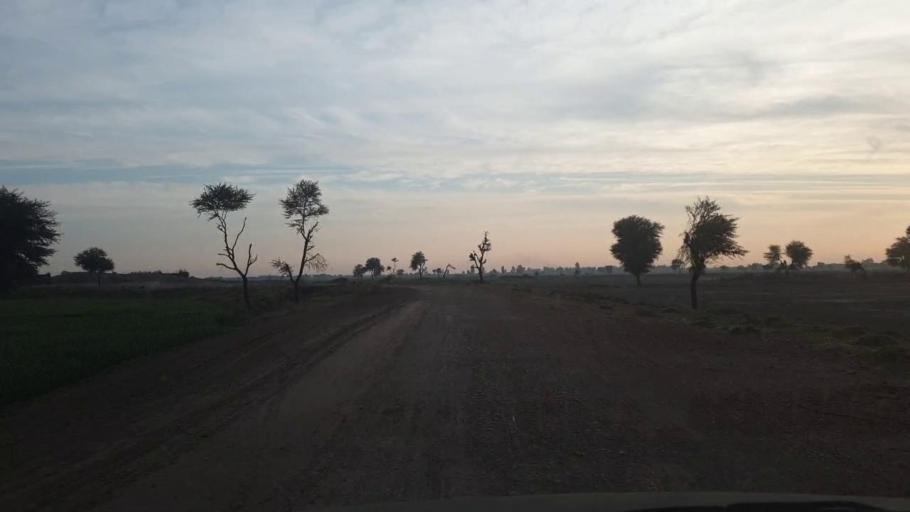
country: PK
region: Sindh
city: Shahpur Chakar
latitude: 26.0577
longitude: 68.5301
